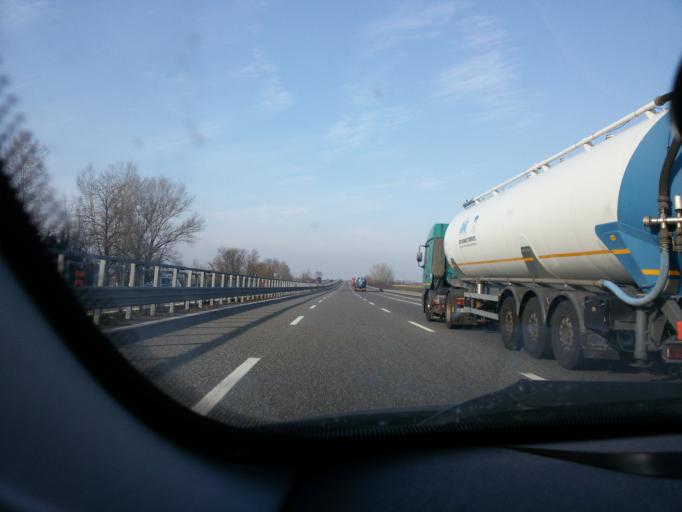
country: IT
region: Piedmont
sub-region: Provincia di Alessandria
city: Mirabello Monferrato
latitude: 45.0183
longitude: 8.5359
